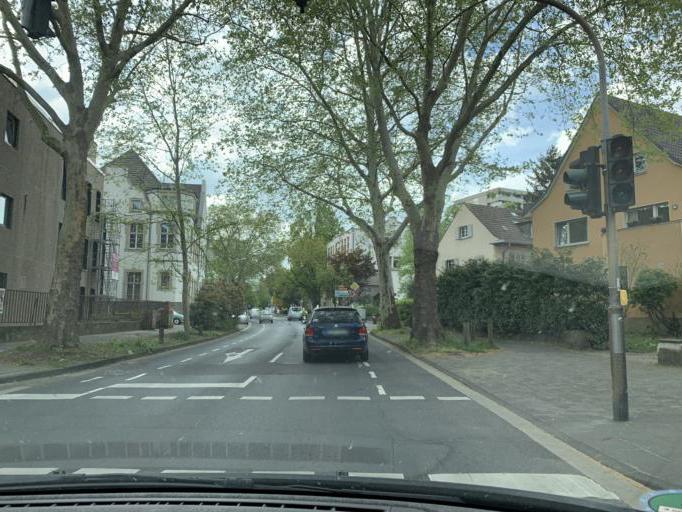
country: DE
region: North Rhine-Westphalia
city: Bruhl
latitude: 50.8311
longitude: 6.9084
